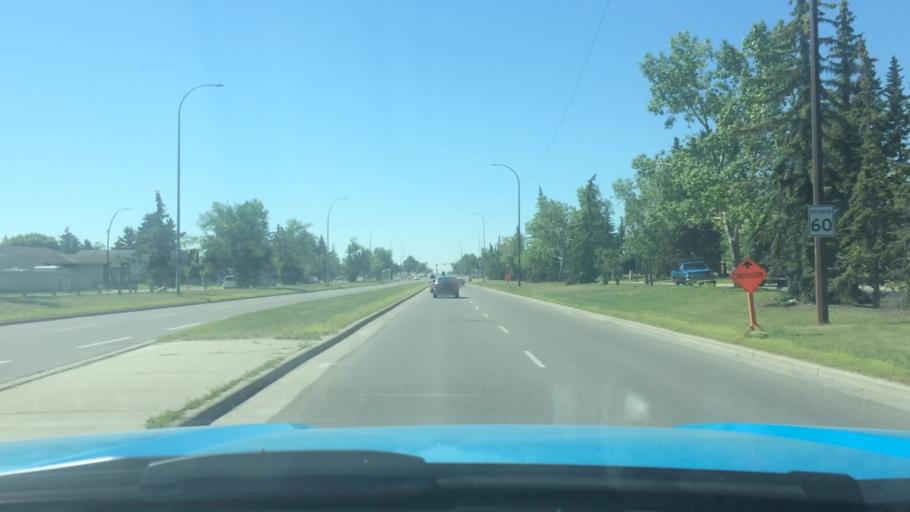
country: CA
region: Alberta
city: Calgary
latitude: 51.0849
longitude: -113.9584
